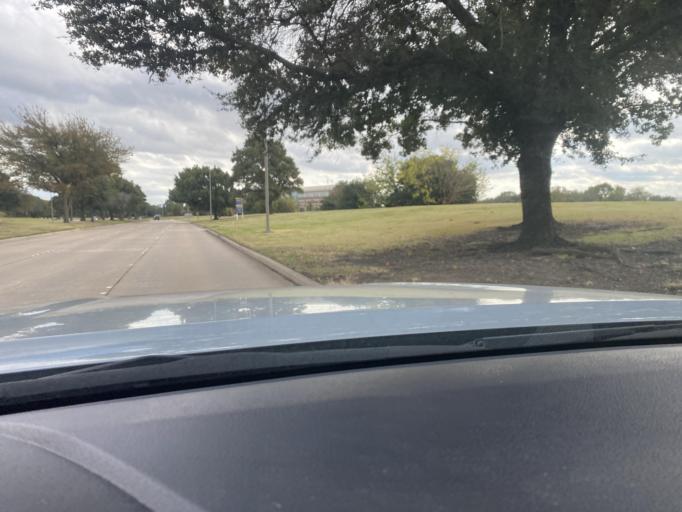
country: US
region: Texas
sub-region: Collin County
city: Frisco
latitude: 33.0738
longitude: -96.8038
